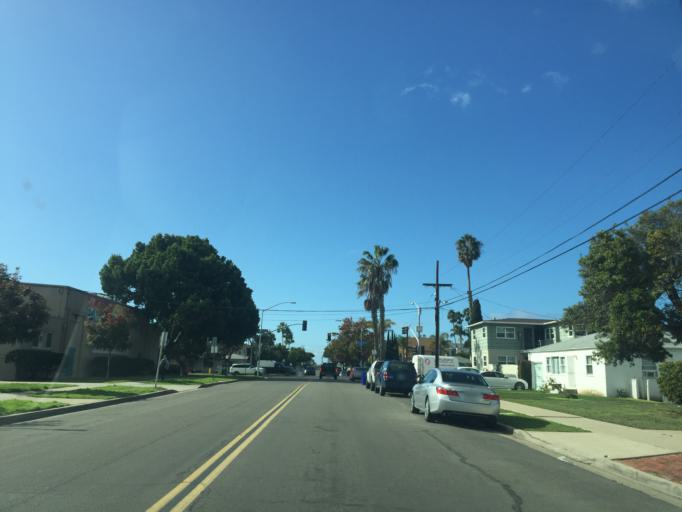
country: US
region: California
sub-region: San Diego County
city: La Jolla
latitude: 32.7942
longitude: -117.2382
